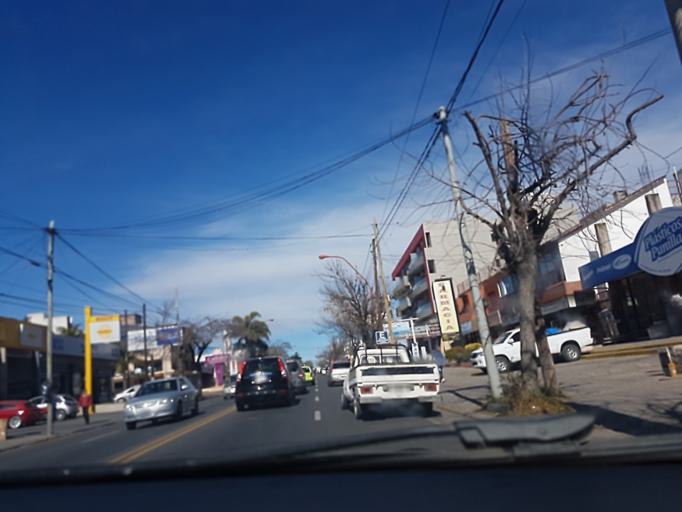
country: AR
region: Cordoba
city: Villa Carlos Paz
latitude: -31.4291
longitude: -64.4967
